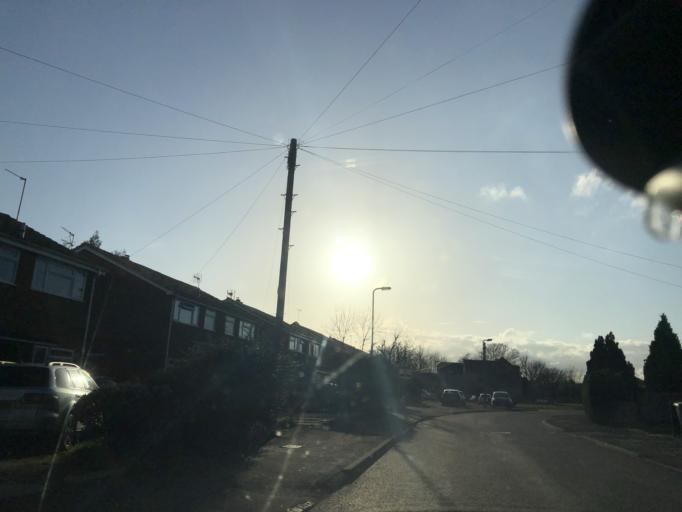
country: GB
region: England
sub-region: Oxfordshire
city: Witney
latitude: 51.7788
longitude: -1.5007
